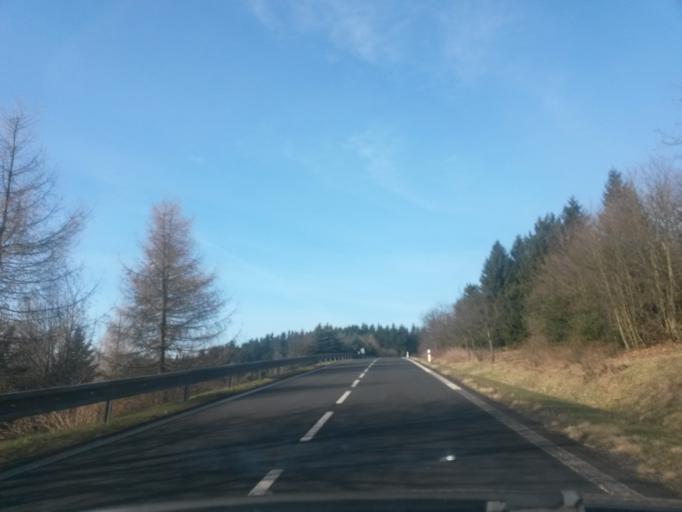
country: CZ
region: Ustecky
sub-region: Okres Chomutov
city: Klasterec nad Ohri
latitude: 50.4613
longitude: 13.2243
